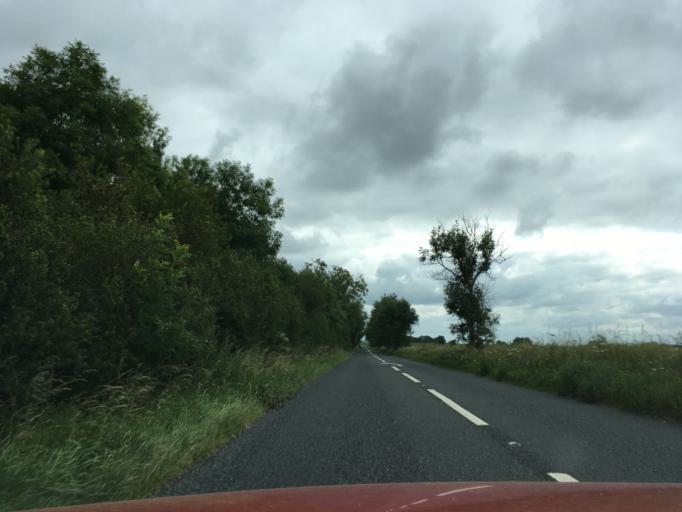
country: GB
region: England
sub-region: Gloucestershire
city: Westfield
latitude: 51.8882
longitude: -1.8517
